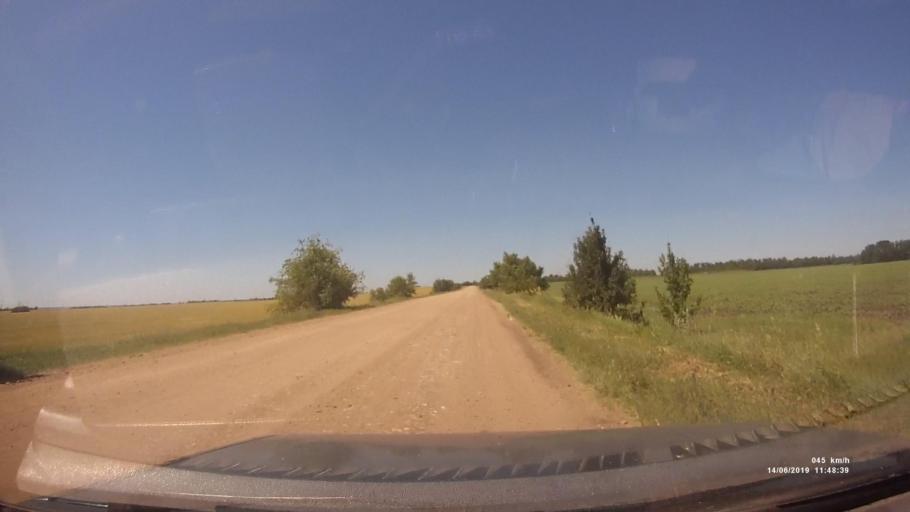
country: RU
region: Rostov
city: Kazanskaya
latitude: 49.8524
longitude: 41.2839
